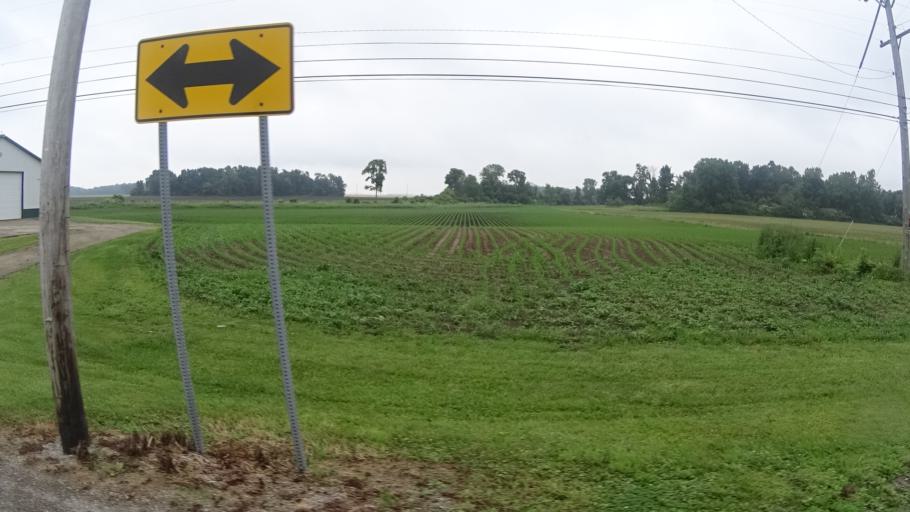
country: US
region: Ohio
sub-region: Huron County
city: Bellevue
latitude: 41.3419
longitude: -82.8166
